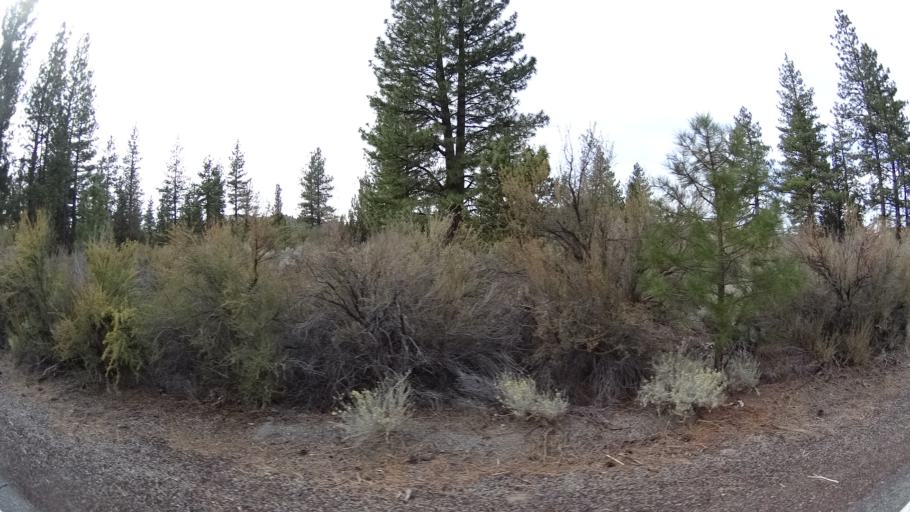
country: US
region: California
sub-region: Siskiyou County
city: Weed
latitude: 41.5469
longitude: -122.2478
